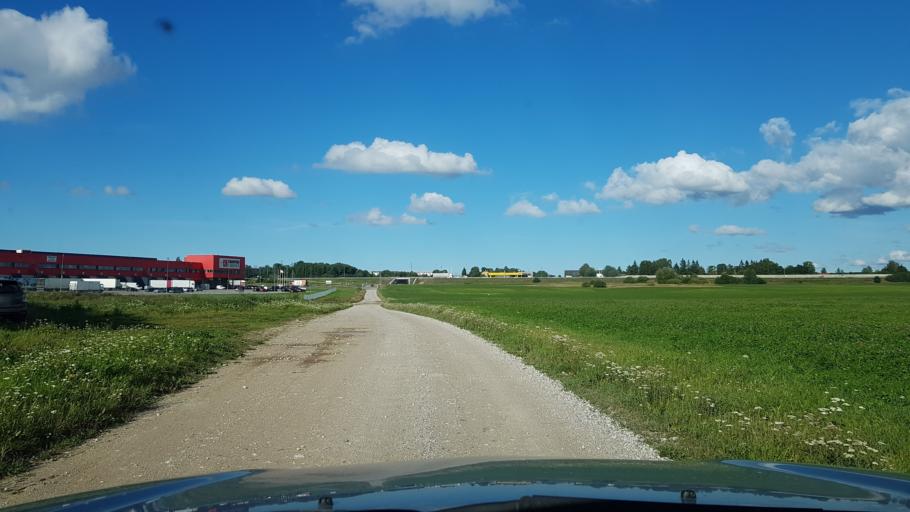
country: EE
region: Harju
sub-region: Rae vald
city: Jueri
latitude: 59.3548
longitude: 24.8669
